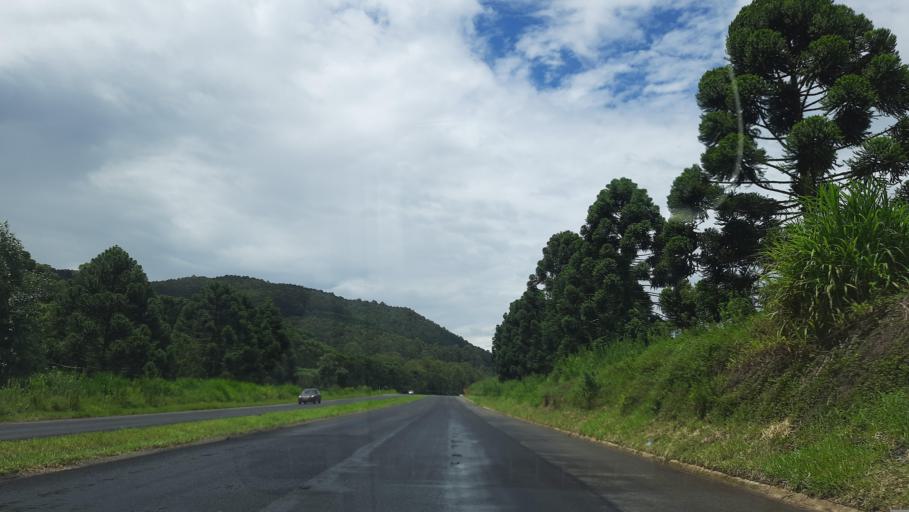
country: BR
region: Minas Gerais
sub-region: Pocos De Caldas
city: Pocos de Caldas
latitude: -21.8079
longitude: -46.6541
